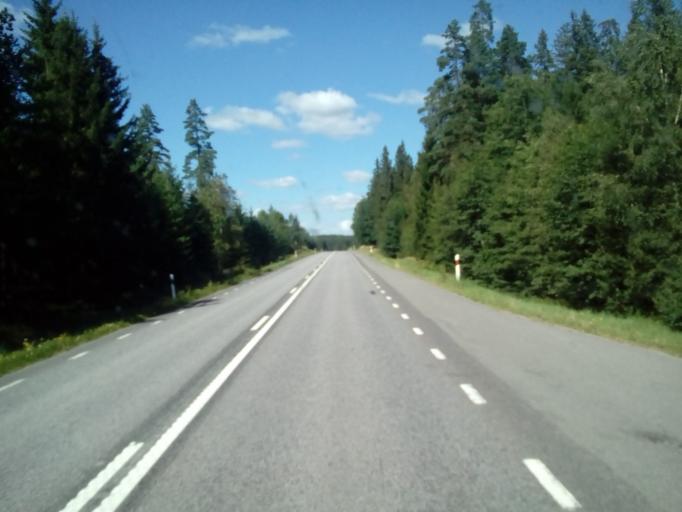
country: SE
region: OEstergoetland
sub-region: Kinda Kommun
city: Rimforsa
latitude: 58.2508
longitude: 15.6002
